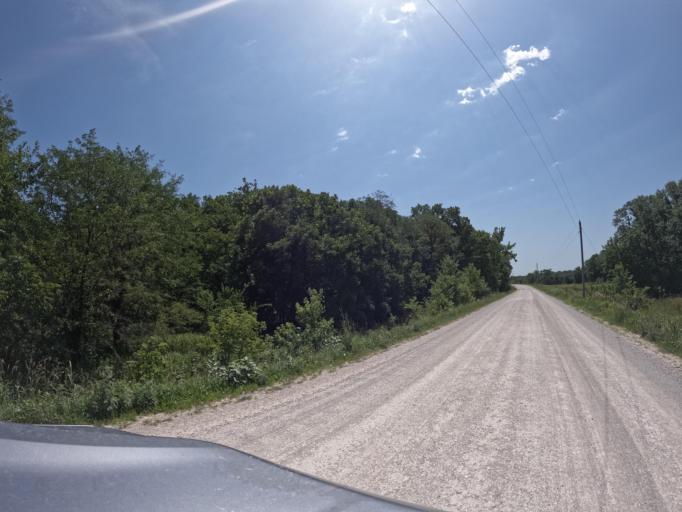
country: US
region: Iowa
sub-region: Henry County
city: Mount Pleasant
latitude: 40.9006
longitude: -91.5518
